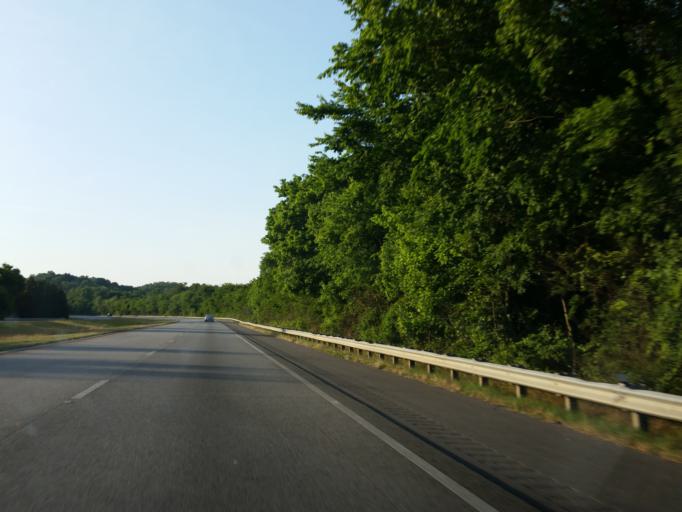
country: US
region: Georgia
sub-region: Dade County
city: Trenton
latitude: 34.7814
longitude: -85.5415
